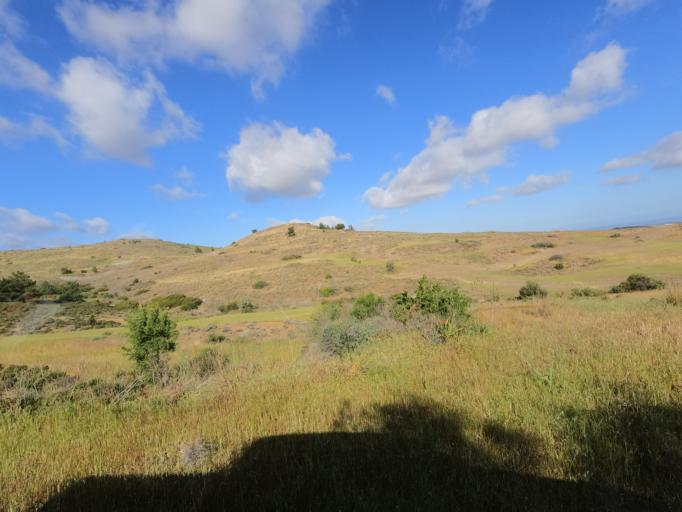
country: CY
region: Lefkosia
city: Peristerona
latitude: 35.0694
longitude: 33.0547
